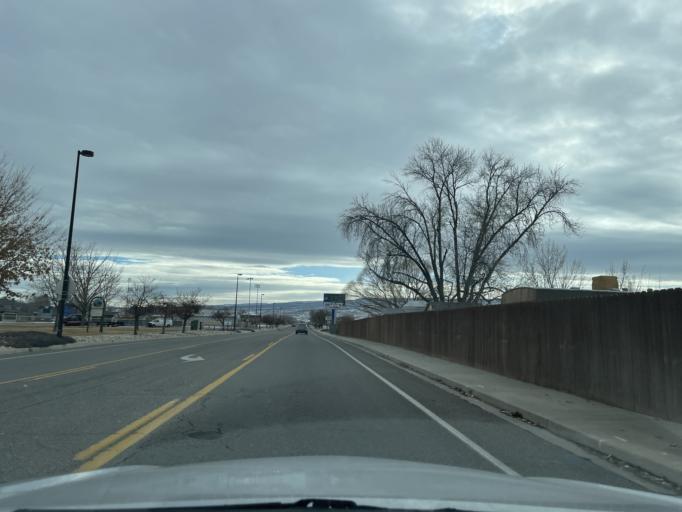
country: US
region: Colorado
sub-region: Mesa County
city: Grand Junction
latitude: 39.0890
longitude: -108.5802
